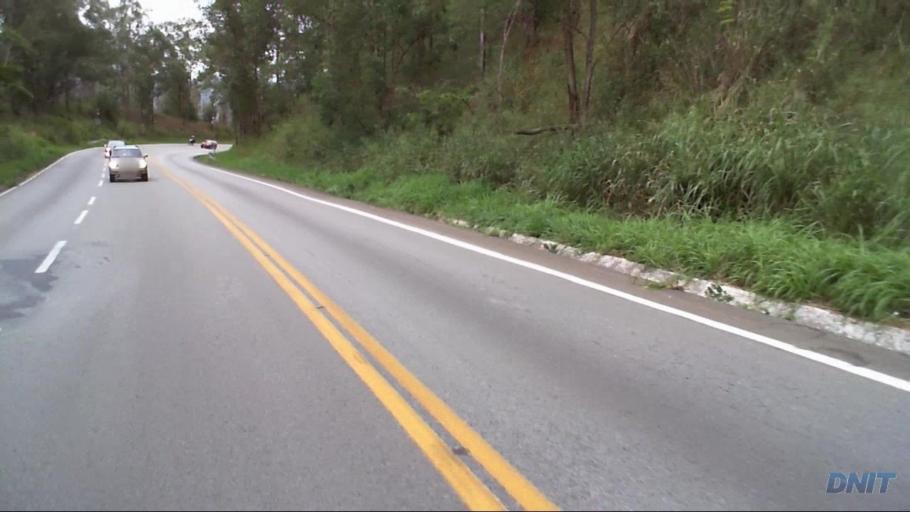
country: BR
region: Minas Gerais
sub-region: Joao Monlevade
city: Joao Monlevade
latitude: -19.8430
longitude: -43.1007
